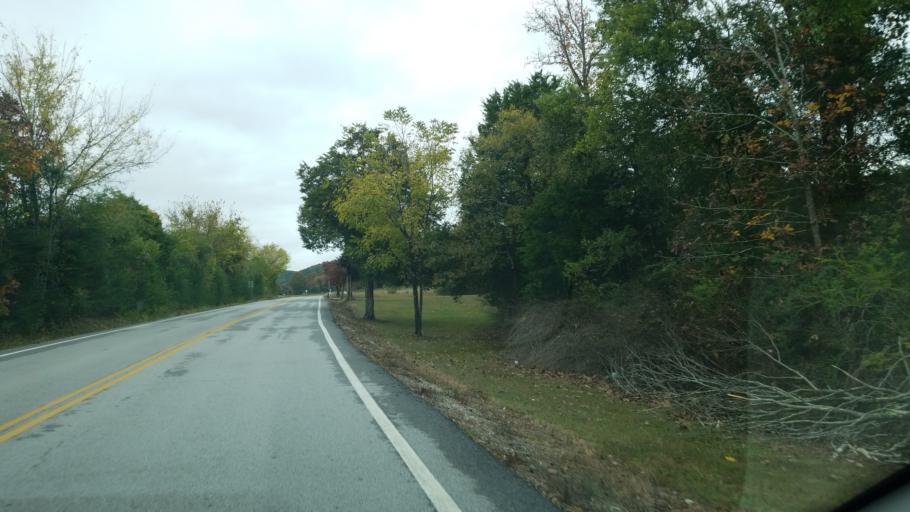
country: US
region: Tennessee
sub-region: Bradley County
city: Hopewell
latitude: 35.2326
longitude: -84.9950
